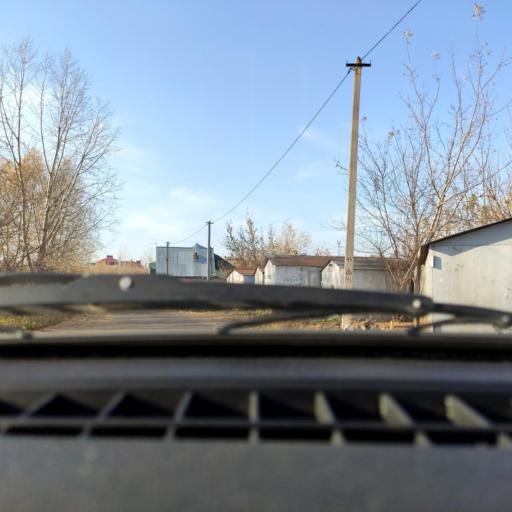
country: RU
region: Bashkortostan
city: Ufa
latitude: 54.8232
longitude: 56.1248
